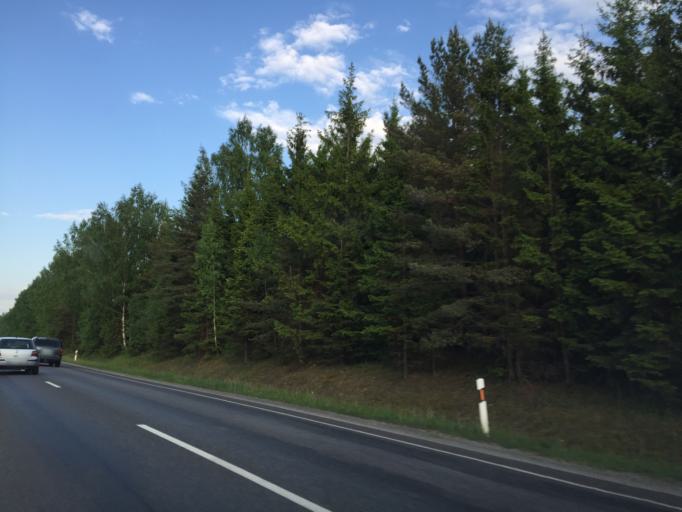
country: LT
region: Telsiu apskritis
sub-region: Telsiai
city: Telsiai
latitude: 56.0025
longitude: 22.1808
